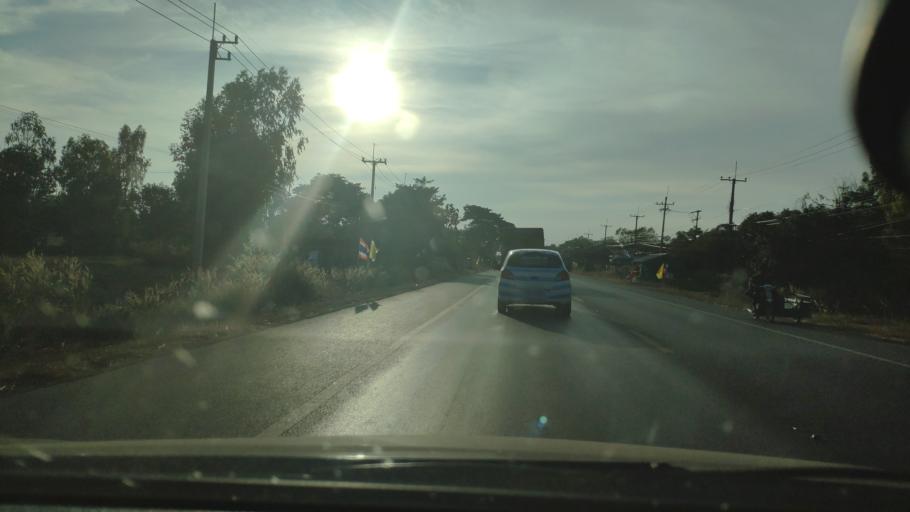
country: TH
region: Roi Et
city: Chiang Khwan
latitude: 16.1038
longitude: 103.8131
